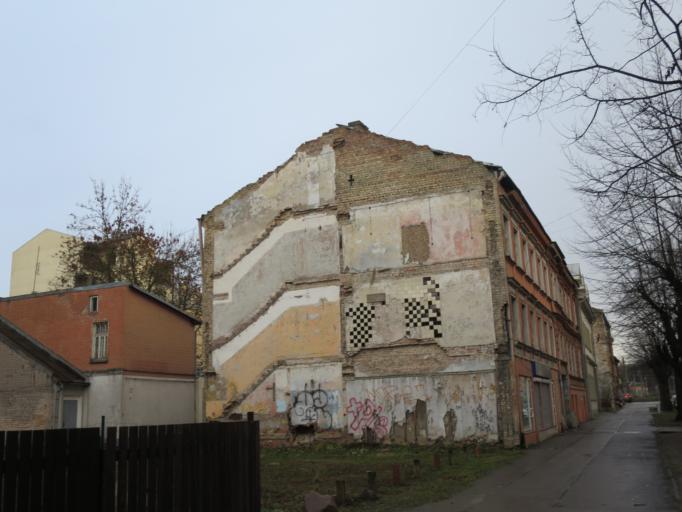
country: LV
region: Riga
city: Riga
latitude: 56.9479
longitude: 24.1400
